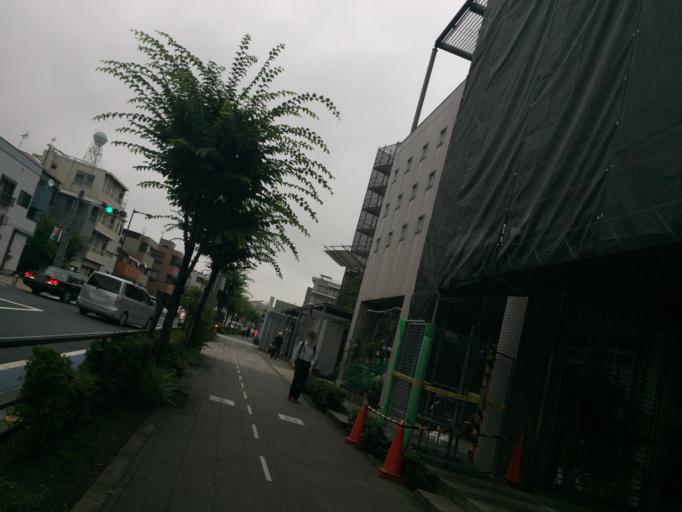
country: JP
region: Tokyo
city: Tokyo
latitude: 35.6388
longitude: 139.6725
